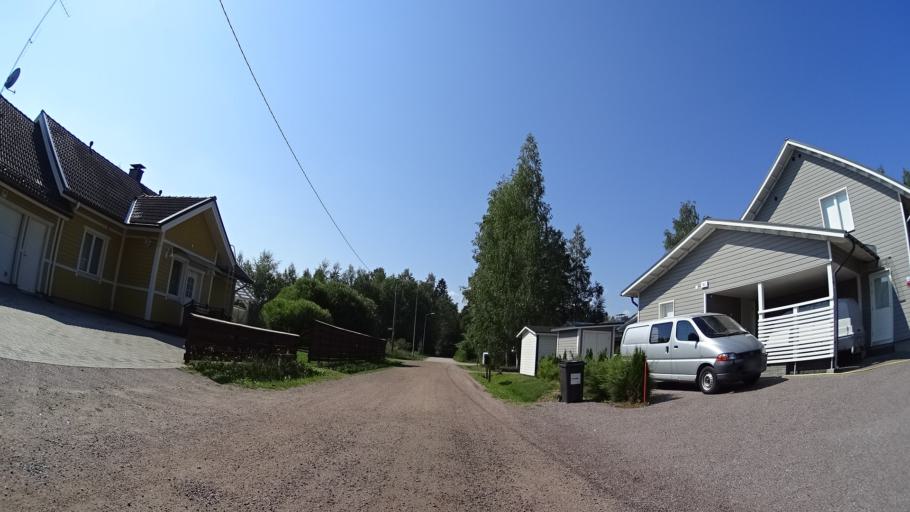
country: FI
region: Uusimaa
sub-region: Helsinki
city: Kerava
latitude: 60.3614
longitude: 25.0742
